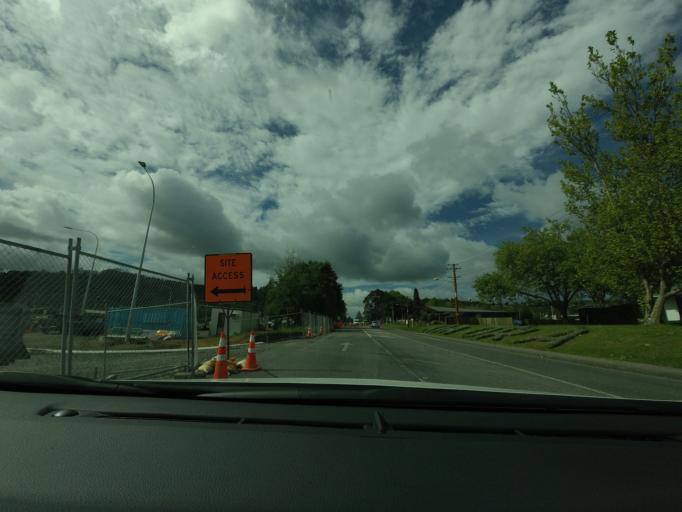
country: NZ
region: Bay of Plenty
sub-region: Rotorua District
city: Rotorua
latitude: -38.1639
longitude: 176.2451
